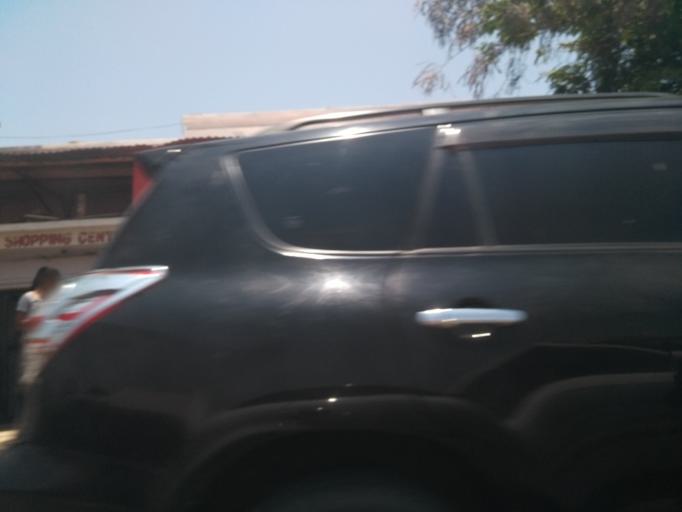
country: TZ
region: Dodoma
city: Dodoma
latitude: -6.1804
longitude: 35.7441
